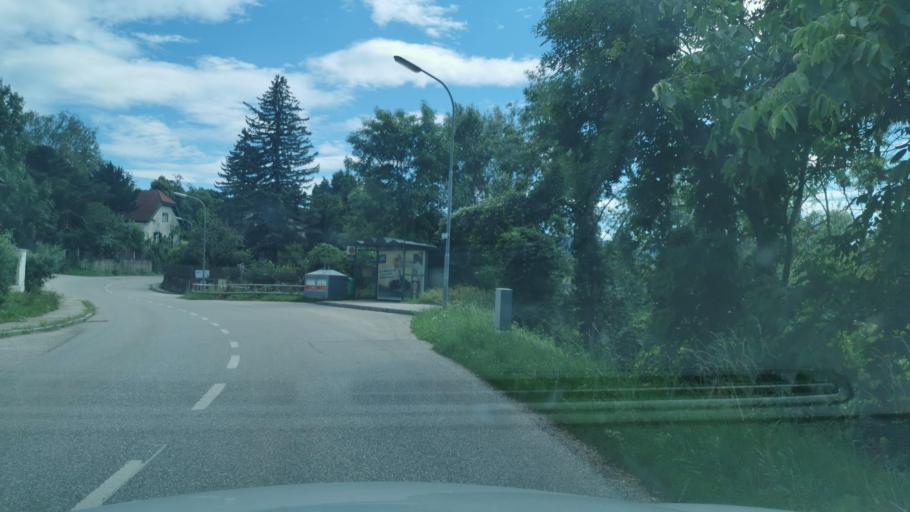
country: AT
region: Lower Austria
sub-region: Politischer Bezirk Sankt Polten
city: Pyhra
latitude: 48.1460
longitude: 15.6403
